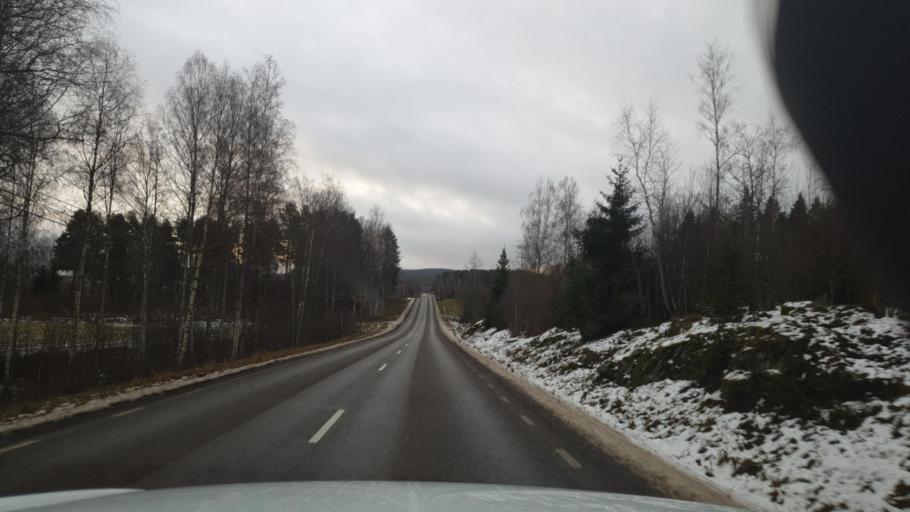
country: SE
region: Vaermland
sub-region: Eda Kommun
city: Amotfors
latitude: 59.7492
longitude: 12.3704
